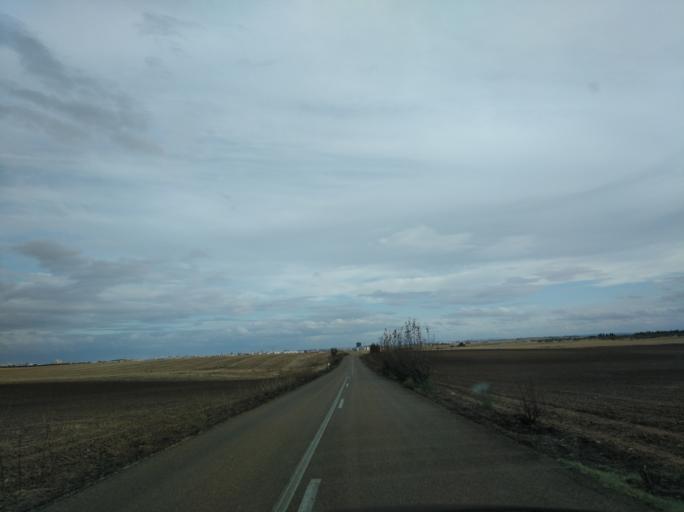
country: ES
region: Extremadura
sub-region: Provincia de Badajoz
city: Badajoz
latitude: 38.9055
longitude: -7.0201
